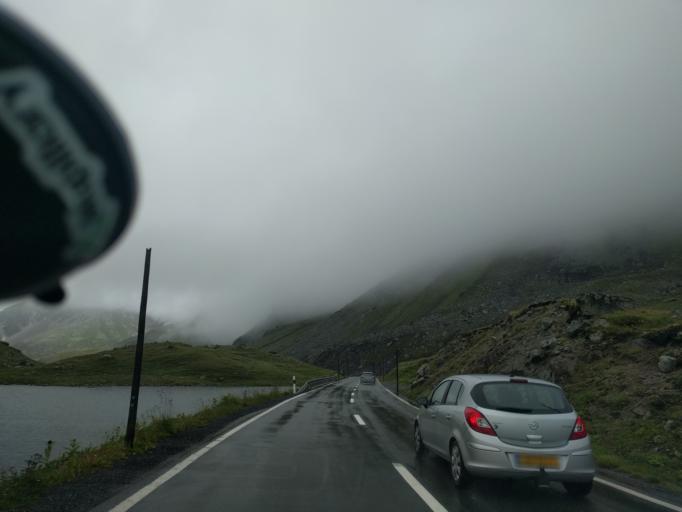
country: CH
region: Grisons
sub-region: Praettigau/Davos District
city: Davos
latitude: 46.7485
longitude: 9.9493
